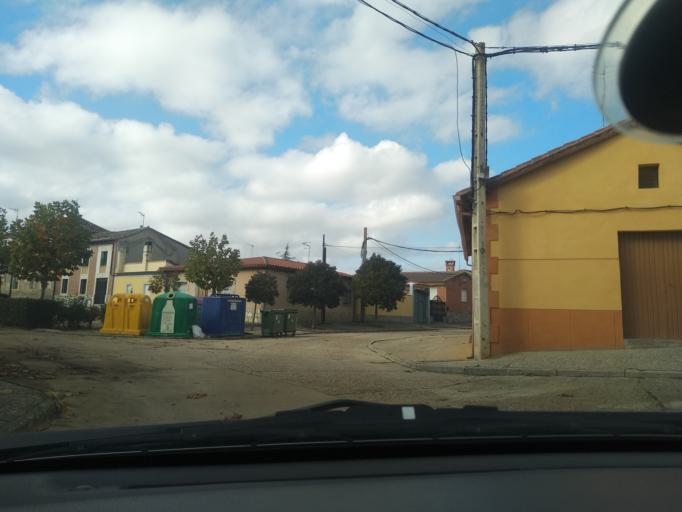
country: ES
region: Castille and Leon
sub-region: Provincia de Valladolid
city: Berrueces
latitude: 41.9451
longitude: -5.0969
